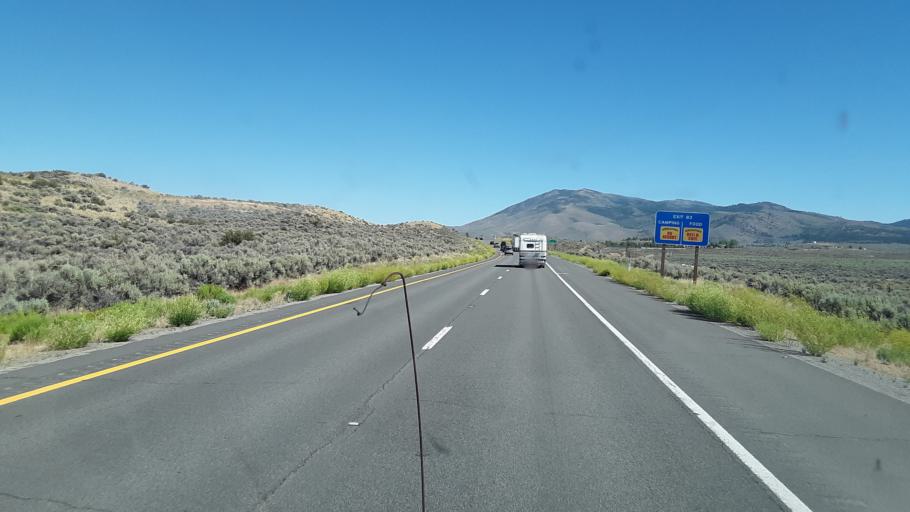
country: US
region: Nevada
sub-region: Washoe County
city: Cold Springs
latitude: 39.6792
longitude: -120.0076
